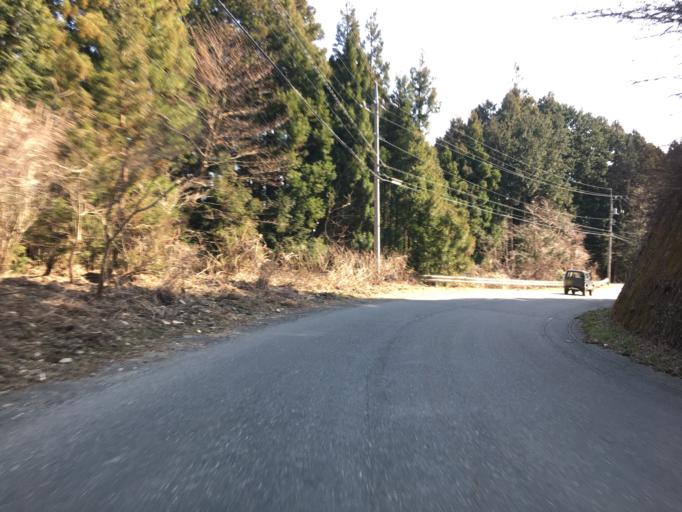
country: JP
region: Ibaraki
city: Takahagi
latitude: 36.8127
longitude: 140.5816
